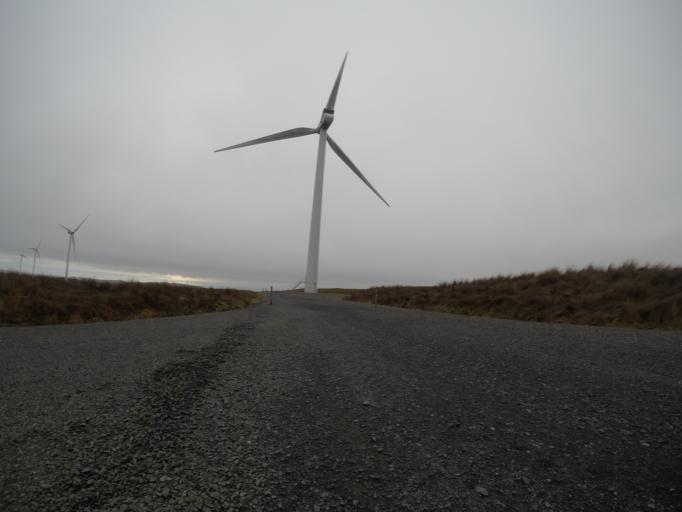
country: GB
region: Scotland
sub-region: North Ayrshire
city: Fairlie
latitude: 55.7412
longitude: -4.7900
